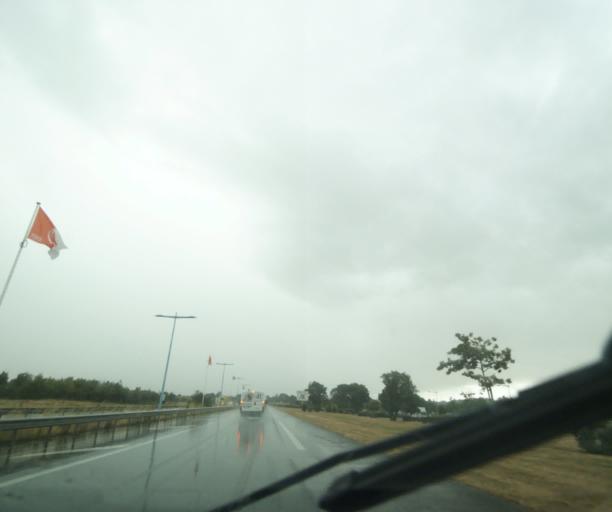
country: FR
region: Pays de la Loire
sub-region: Departement de la Vendee
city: Chateau-d'Olonne
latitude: 46.5166
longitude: -1.7525
